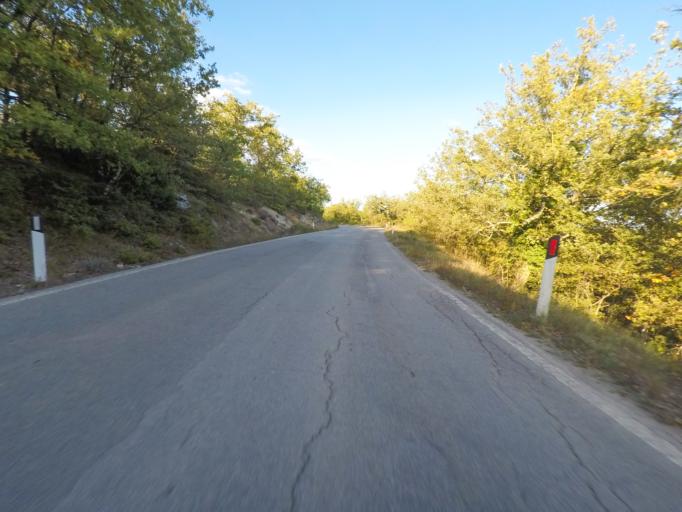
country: IT
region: Tuscany
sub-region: Provincia di Siena
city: Radda in Chianti
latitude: 43.4446
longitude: 11.3943
